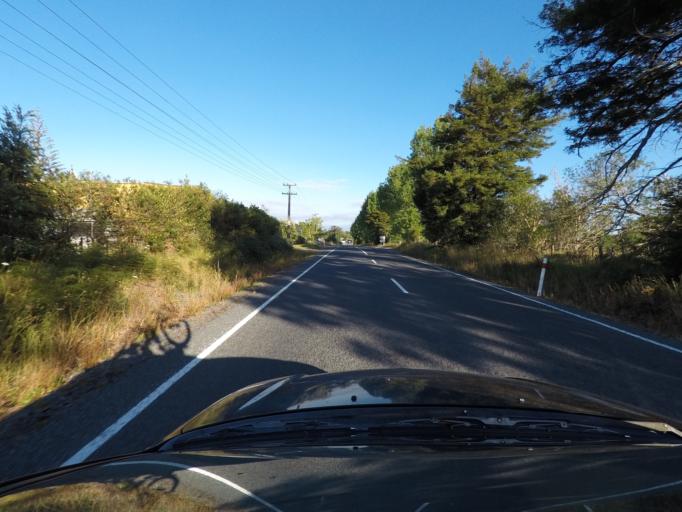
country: NZ
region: Northland
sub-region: Whangarei
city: Whangarei
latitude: -35.6448
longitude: 174.3018
